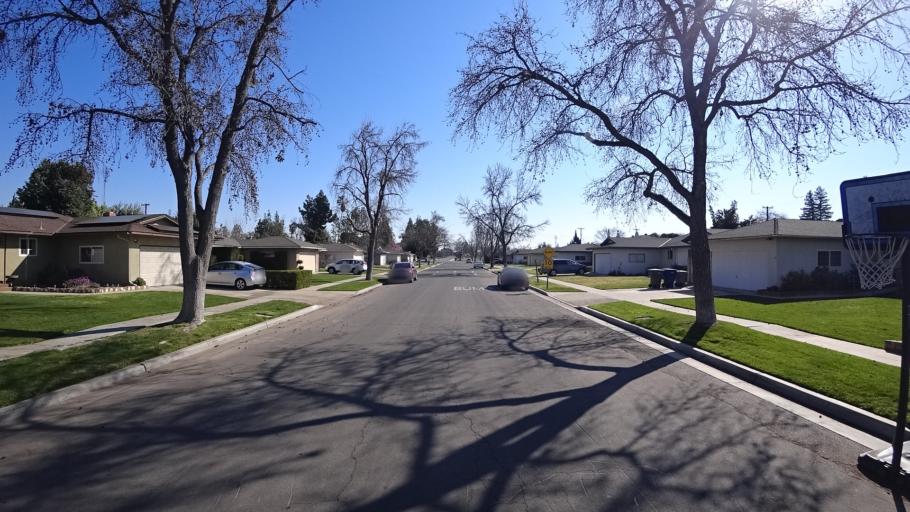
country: US
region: California
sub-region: Fresno County
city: Clovis
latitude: 36.8265
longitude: -119.7742
